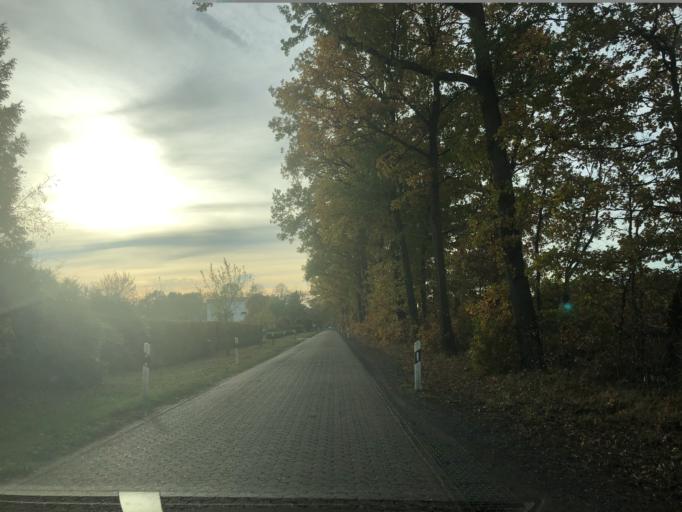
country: DE
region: Lower Saxony
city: Edewecht
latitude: 53.0928
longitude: 8.0803
